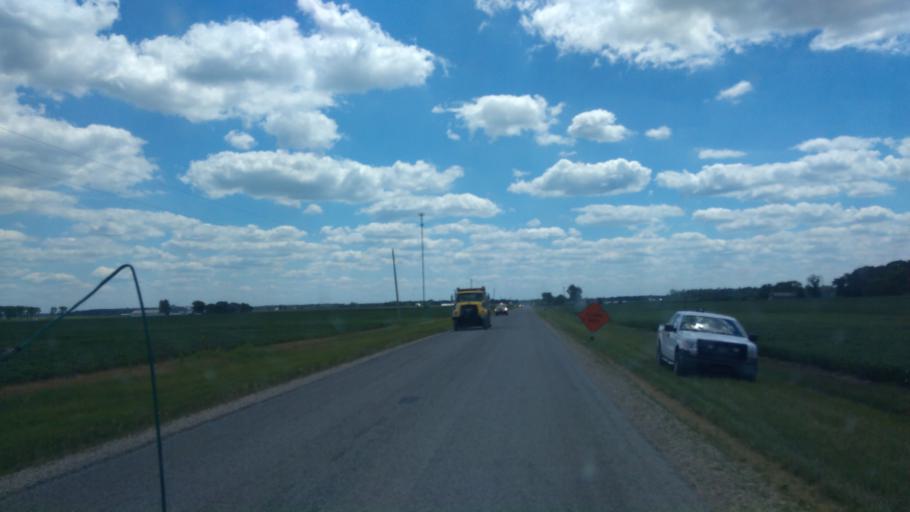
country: US
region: Indiana
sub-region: Adams County
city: Geneva
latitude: 40.5971
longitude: -85.0407
